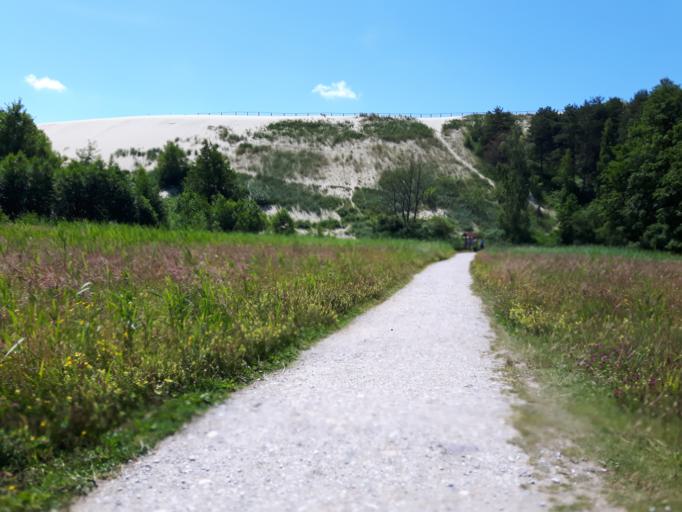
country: LT
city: Nida
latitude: 55.2963
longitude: 20.9955
